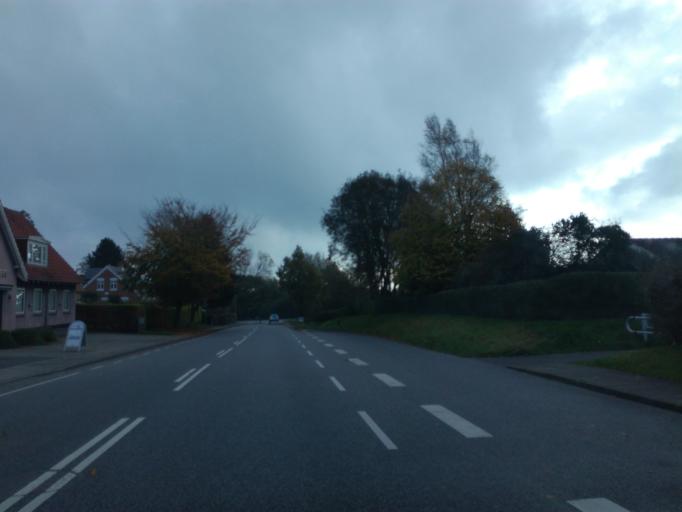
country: DK
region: South Denmark
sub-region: Vejle Kommune
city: Vejle
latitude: 55.6757
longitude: 9.5696
